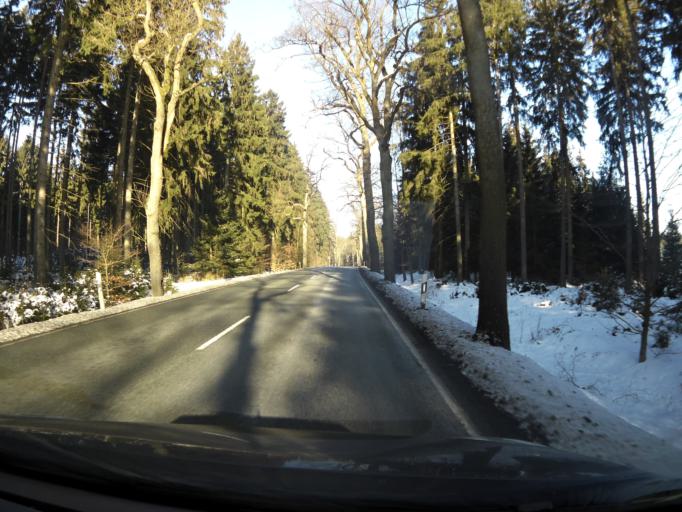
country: DE
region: Thuringia
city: Schleiz
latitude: 50.5397
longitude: 11.8101
